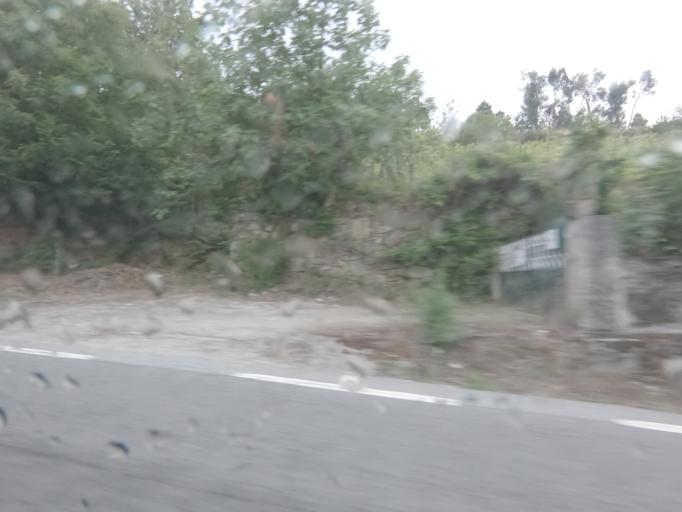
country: PT
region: Viseu
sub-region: Armamar
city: Armamar
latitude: 41.1301
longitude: -7.7398
